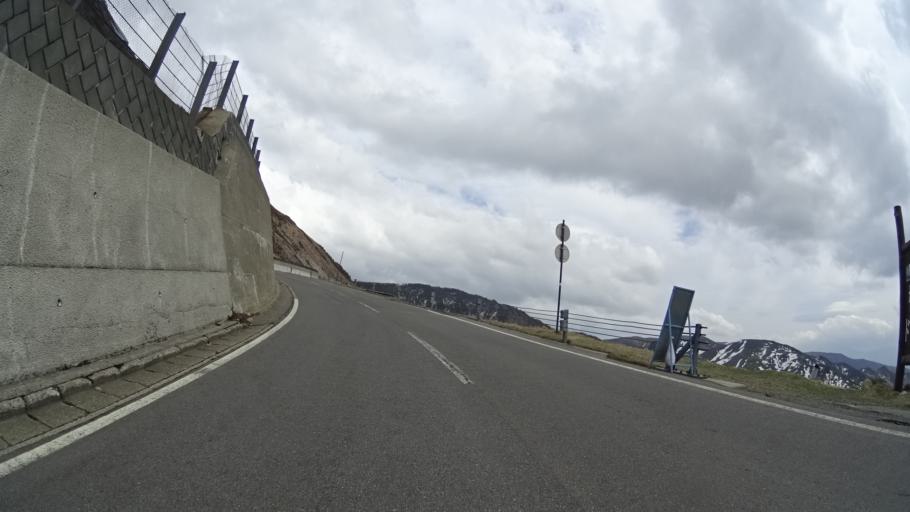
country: JP
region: Nagano
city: Nakano
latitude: 36.6690
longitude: 138.5190
